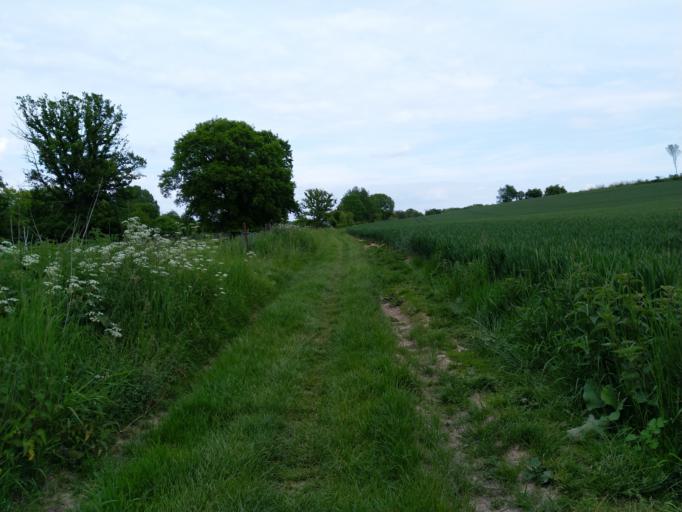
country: FR
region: Picardie
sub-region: Departement de l'Aisne
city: Guise
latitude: 49.9280
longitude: 3.6071
